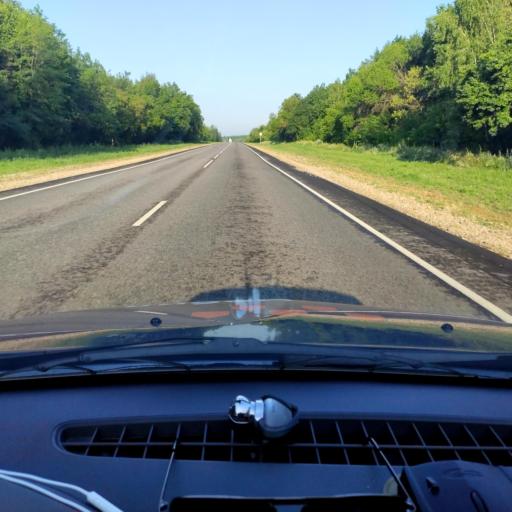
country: RU
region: Lipetsk
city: Izmalkovo
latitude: 52.4495
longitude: 37.9898
